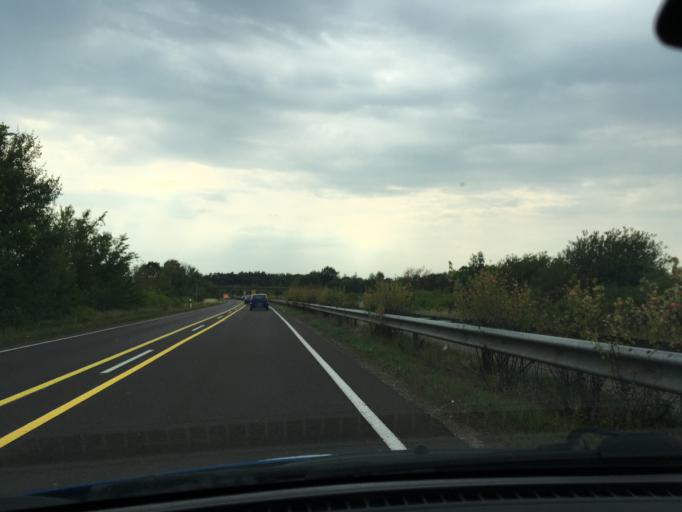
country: DE
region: Lower Saxony
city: Burgdorf
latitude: 52.4659
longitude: 9.9602
